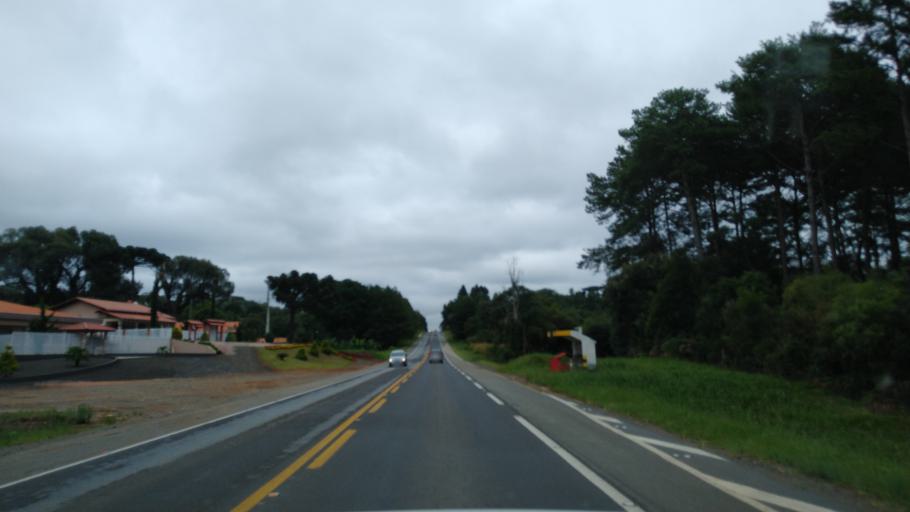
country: BR
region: Santa Catarina
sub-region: Tres Barras
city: Tres Barras
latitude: -26.1696
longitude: -50.1498
